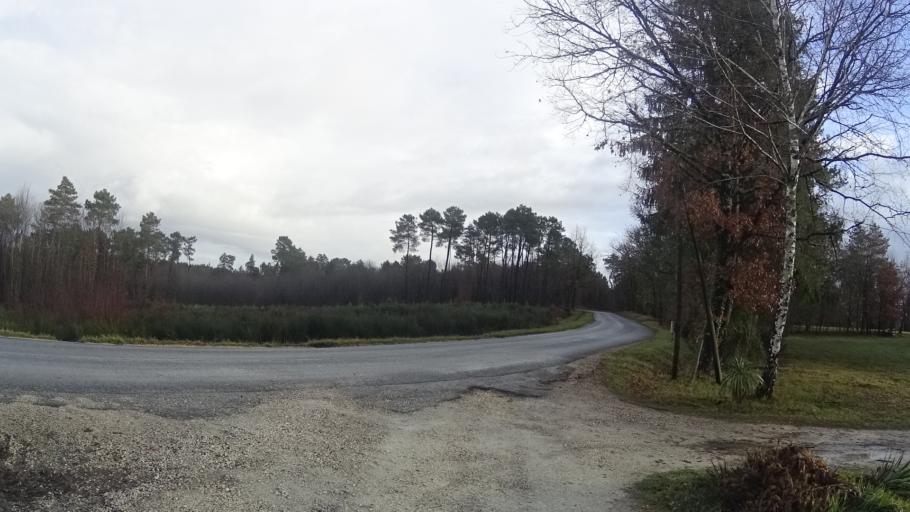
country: FR
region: Aquitaine
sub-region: Departement de la Dordogne
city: Antonne-et-Trigonant
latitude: 45.2223
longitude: 0.8900
